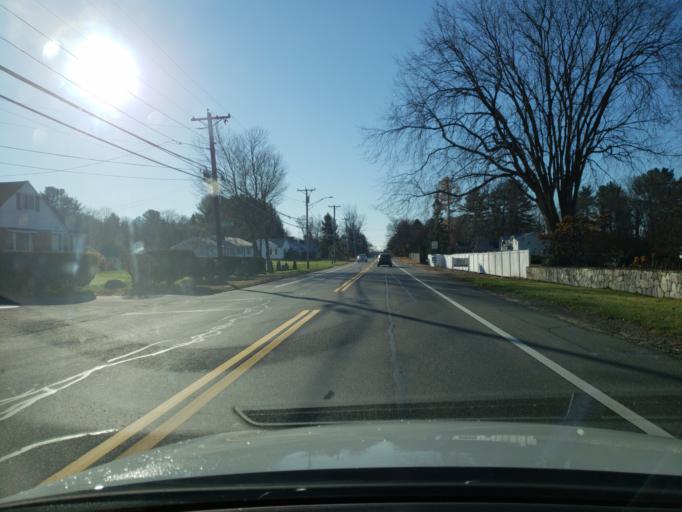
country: US
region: Massachusetts
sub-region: Essex County
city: Andover
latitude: 42.6249
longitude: -71.1263
